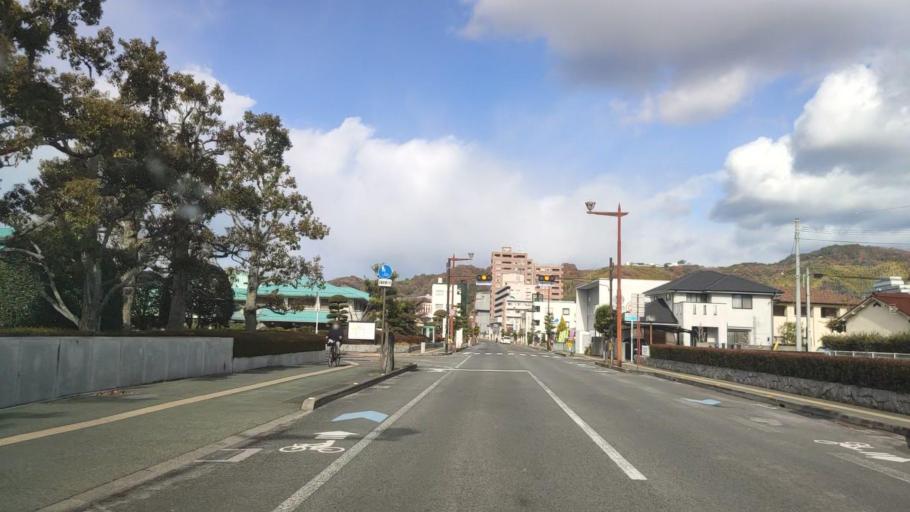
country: JP
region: Ehime
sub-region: Shikoku-chuo Shi
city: Matsuyama
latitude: 33.8490
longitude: 132.7806
